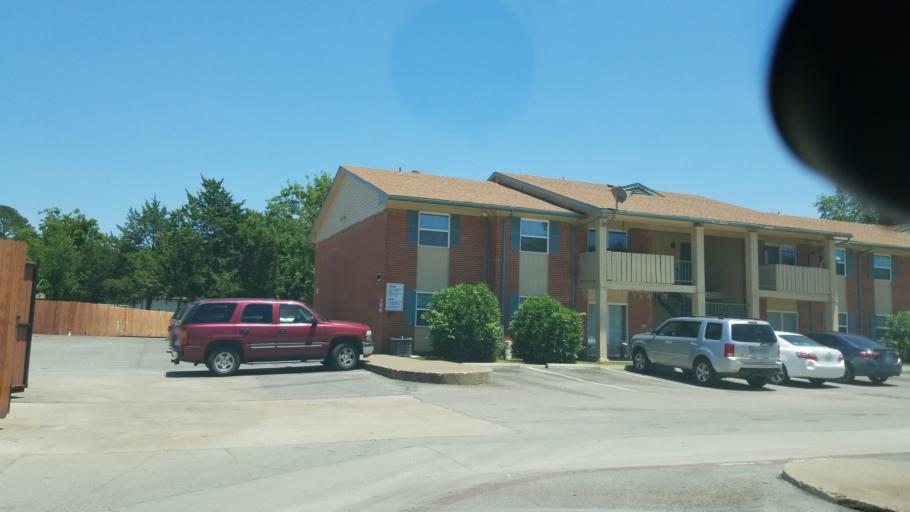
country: US
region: Texas
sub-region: Dallas County
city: Irving
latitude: 32.8252
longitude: -96.9339
